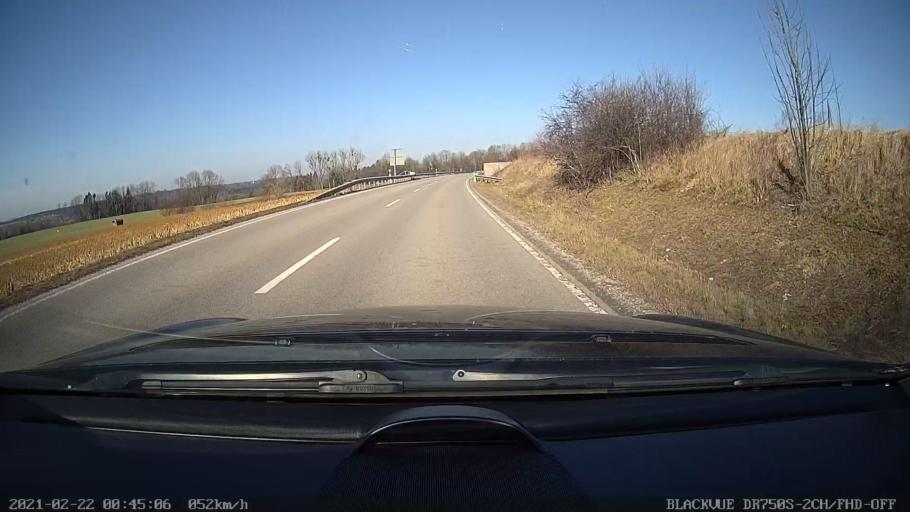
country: DE
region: Bavaria
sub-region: Upper Bavaria
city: Griesstatt
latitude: 47.9907
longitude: 12.1737
